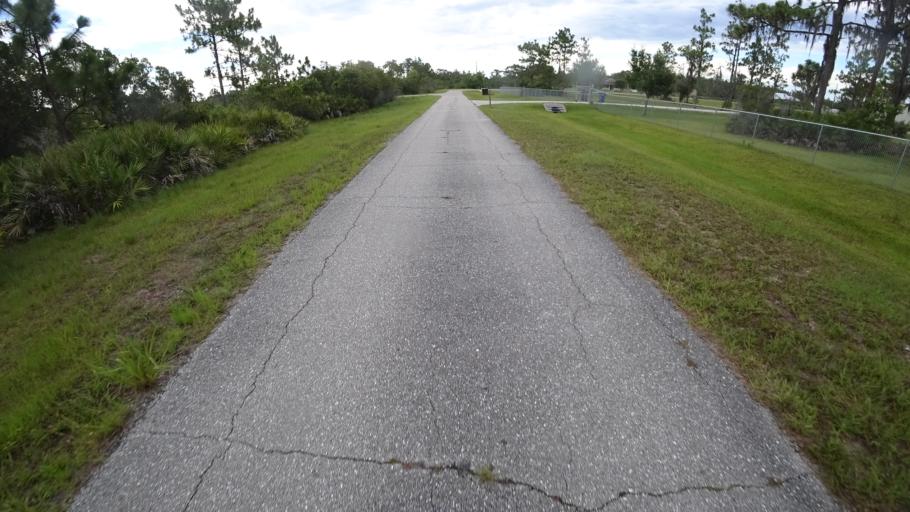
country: US
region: Florida
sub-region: Sarasota County
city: The Meadows
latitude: 27.4124
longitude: -82.2844
